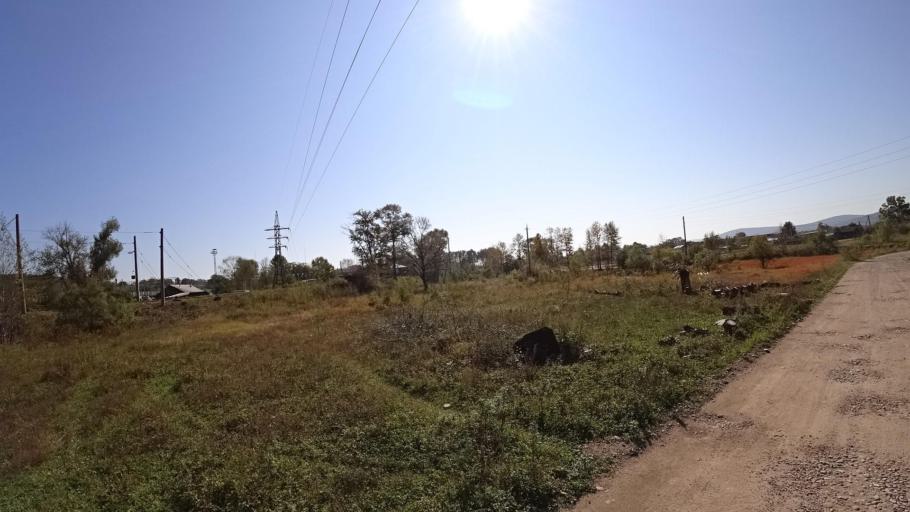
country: RU
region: Jewish Autonomous Oblast
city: Bira
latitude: 49.0014
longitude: 132.4510
